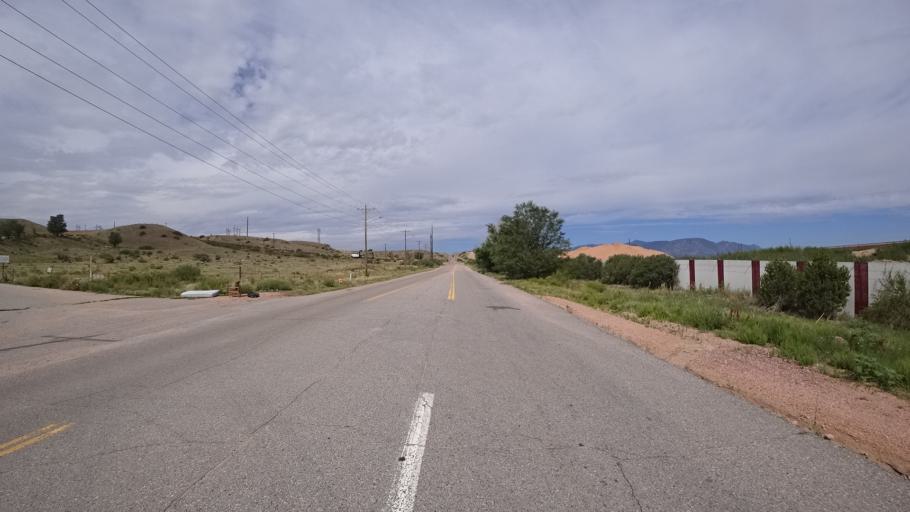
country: US
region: Colorado
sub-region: El Paso County
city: Fountain
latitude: 38.6682
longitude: -104.7164
